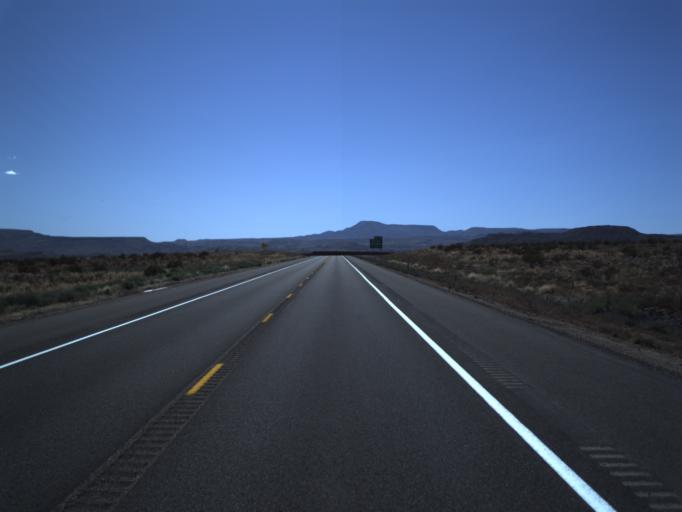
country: US
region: Utah
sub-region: Washington County
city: Washington
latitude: 37.0333
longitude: -113.4852
